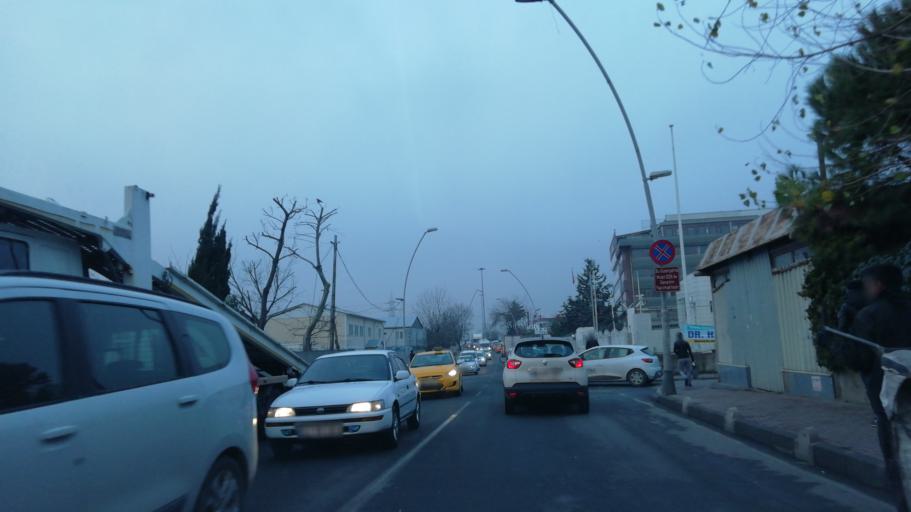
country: TR
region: Istanbul
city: Bahcelievler
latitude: 41.0009
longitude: 28.8248
